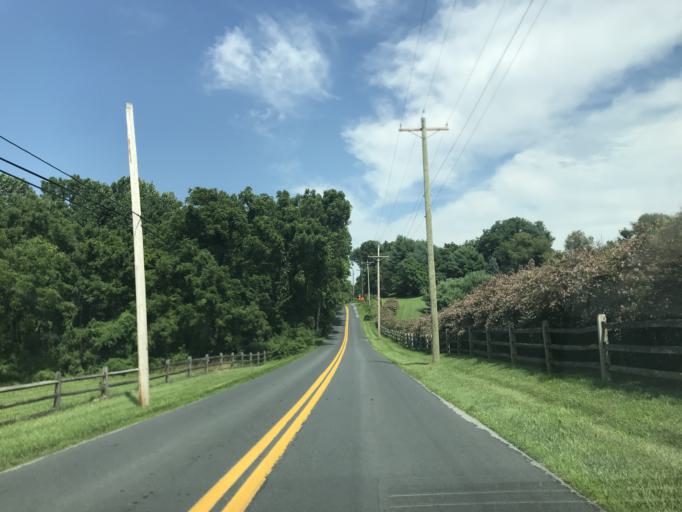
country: US
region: Delaware
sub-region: New Castle County
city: Greenville
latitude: 39.8192
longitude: -75.6077
